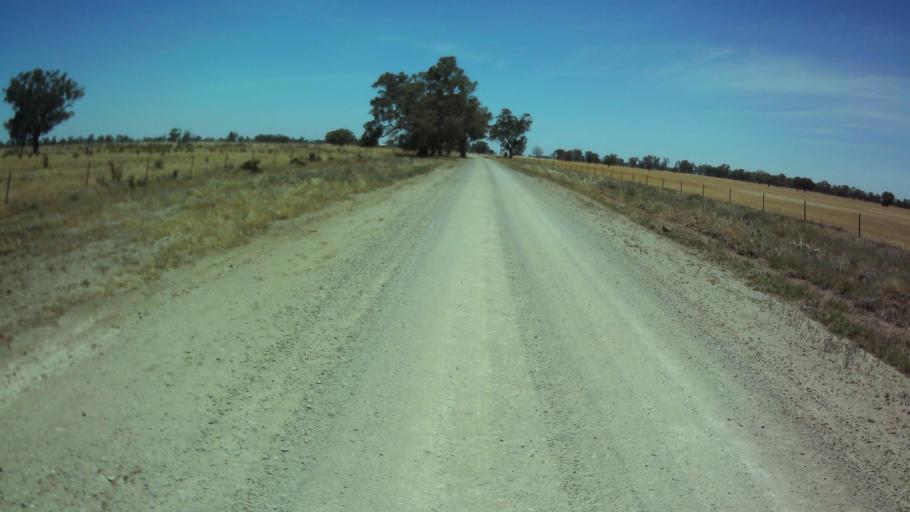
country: AU
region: New South Wales
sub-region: Weddin
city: Grenfell
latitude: -33.9996
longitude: 147.7370
